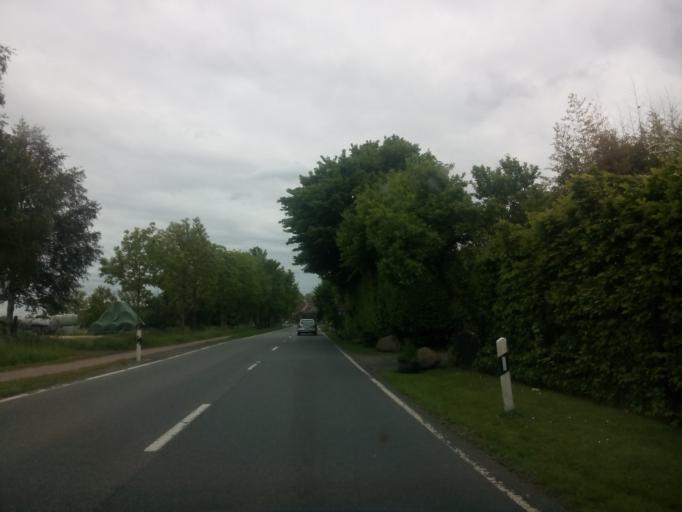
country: DE
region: Lower Saxony
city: Stuhr
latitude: 53.0816
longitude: 8.7061
